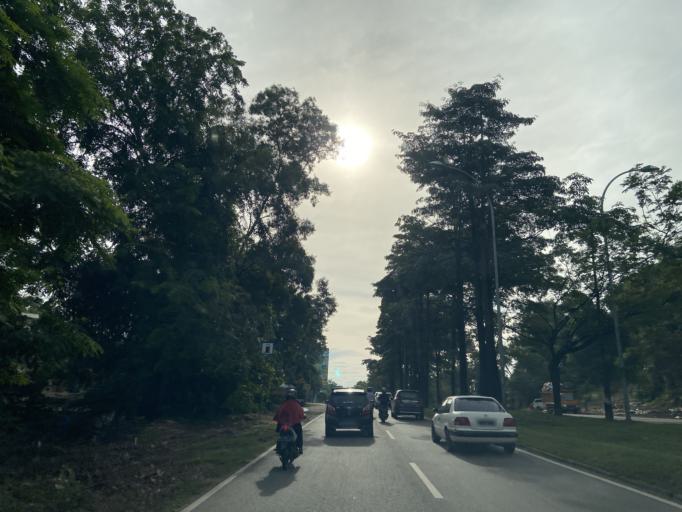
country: SG
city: Singapore
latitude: 1.1324
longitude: 104.0201
